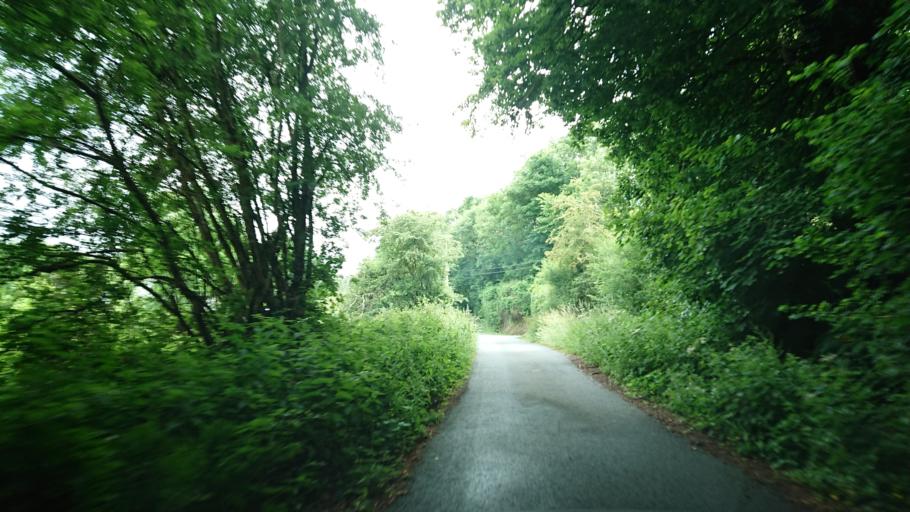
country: IE
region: Munster
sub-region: Waterford
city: Waterford
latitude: 52.2732
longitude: -7.1464
